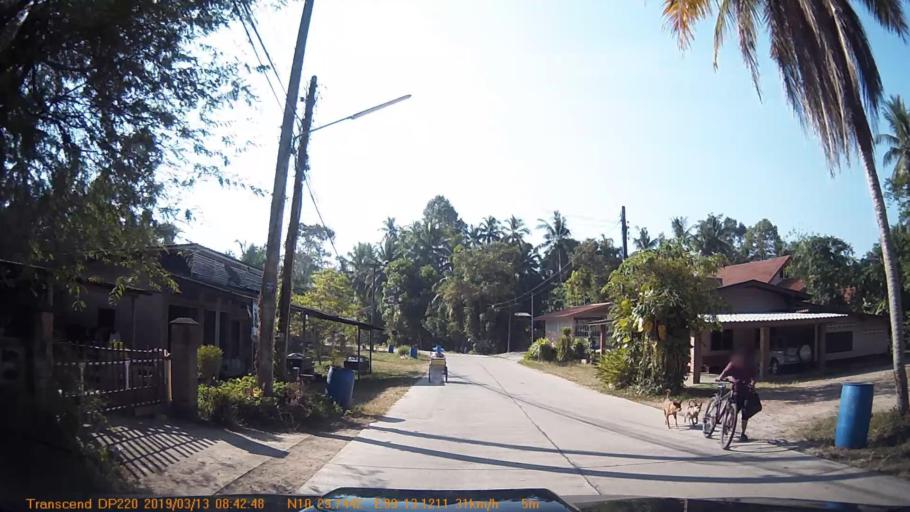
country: TH
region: Chumphon
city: Chumphon
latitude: 10.4956
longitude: 99.2188
